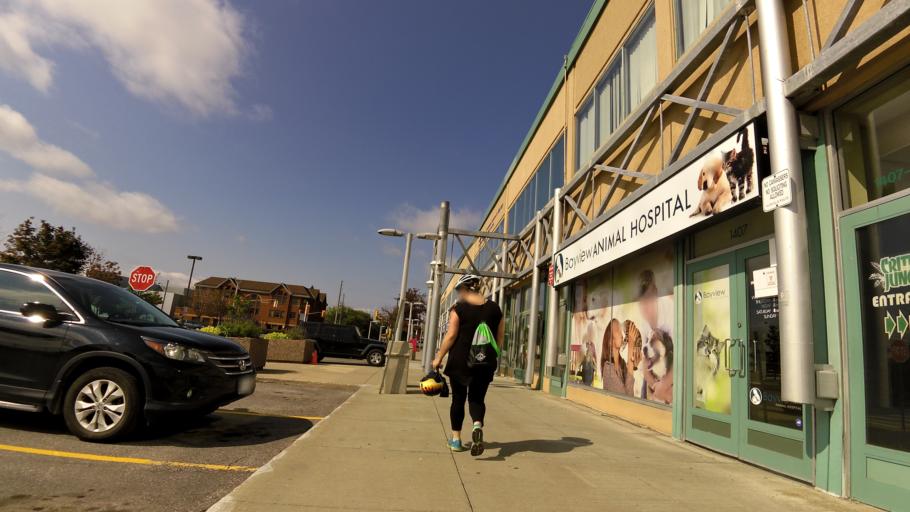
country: CA
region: Ontario
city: Ottawa
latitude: 45.3861
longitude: -75.7399
